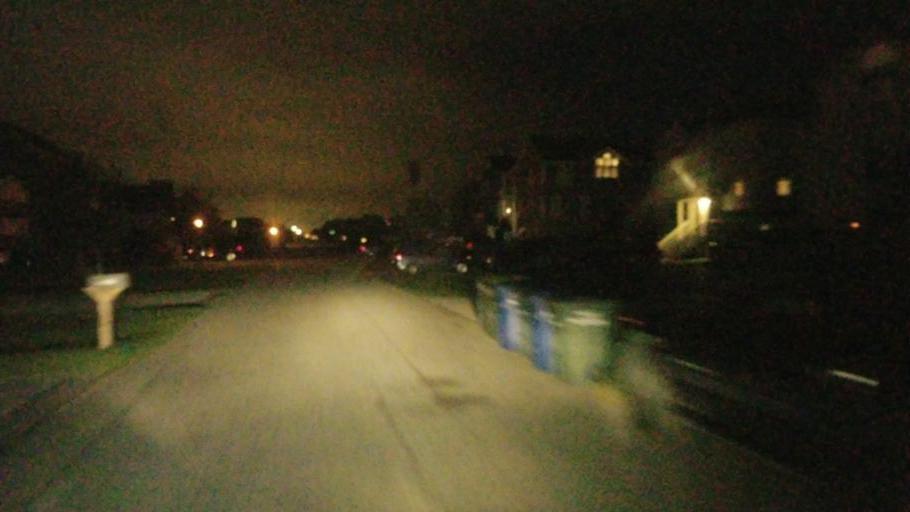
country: US
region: North Carolina
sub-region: Dare County
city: Nags Head
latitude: 35.9850
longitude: -75.6413
